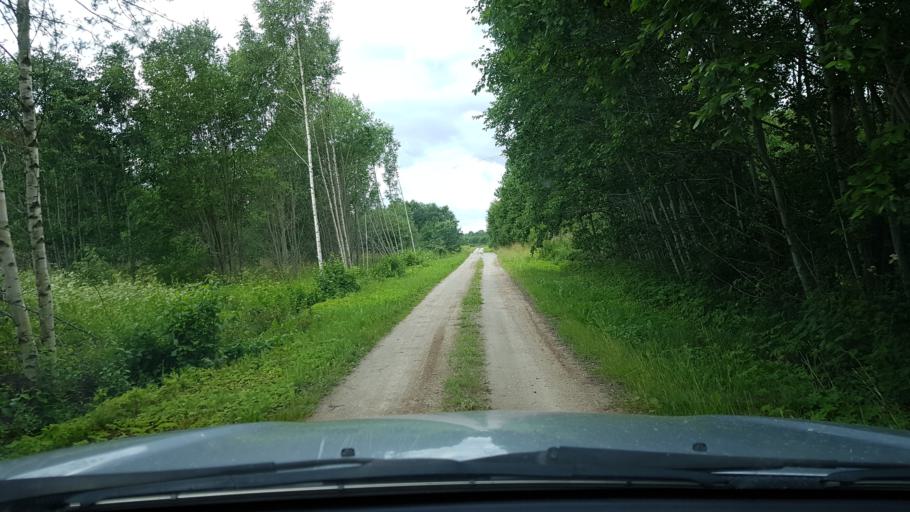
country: EE
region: Ida-Virumaa
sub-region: Narva-Joesuu linn
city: Narva-Joesuu
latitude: 59.4048
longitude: 27.9709
